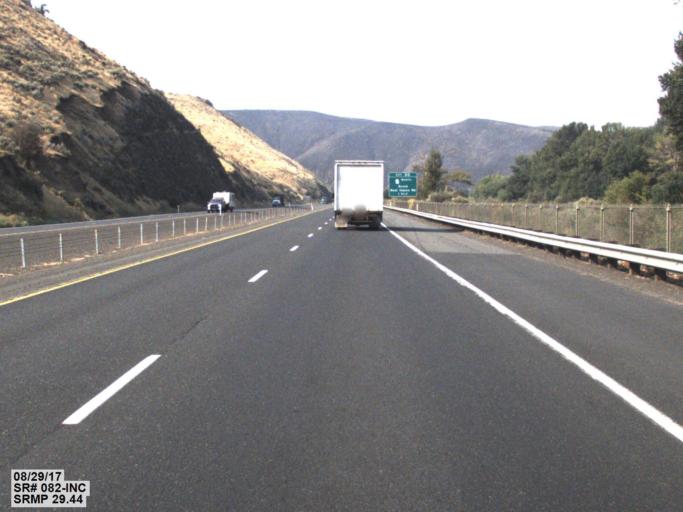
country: US
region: Washington
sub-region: Yakima County
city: Selah
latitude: 46.6443
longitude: -120.5107
